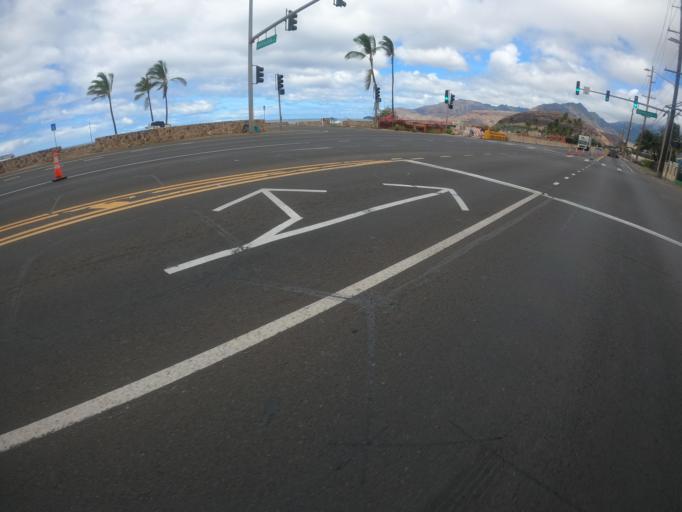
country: US
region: Hawaii
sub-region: Honolulu County
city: Ma'ili
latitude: 21.4083
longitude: -158.1772
